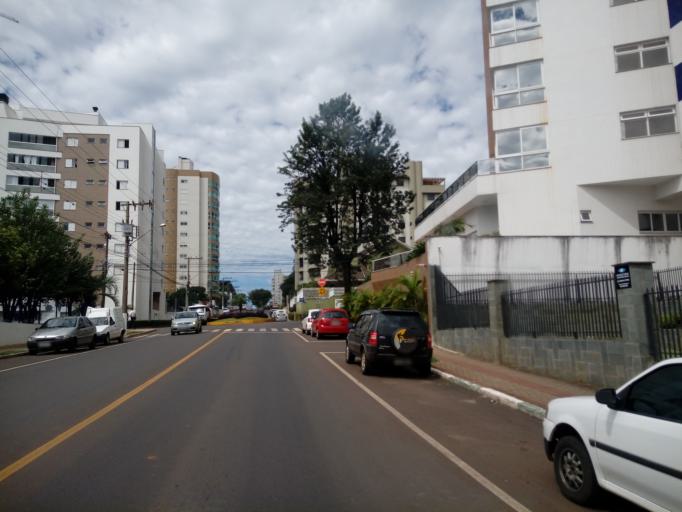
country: BR
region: Santa Catarina
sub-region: Chapeco
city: Chapeco
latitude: -27.1011
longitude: -52.6087
